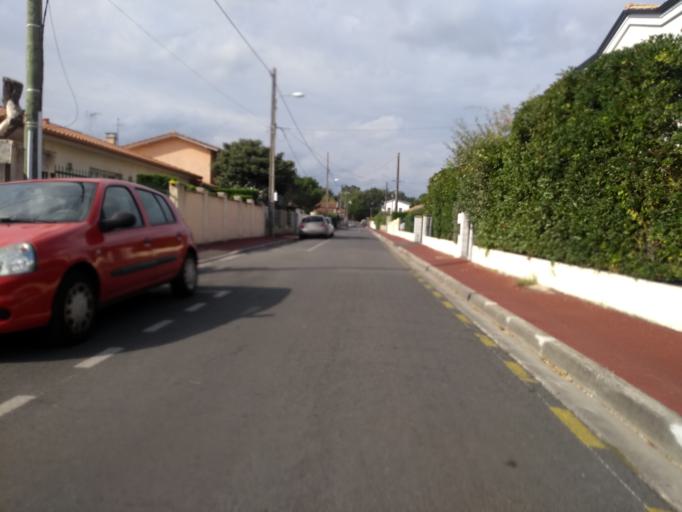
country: FR
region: Aquitaine
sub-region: Departement de la Gironde
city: Pessac
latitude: 44.8161
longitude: -0.6283
